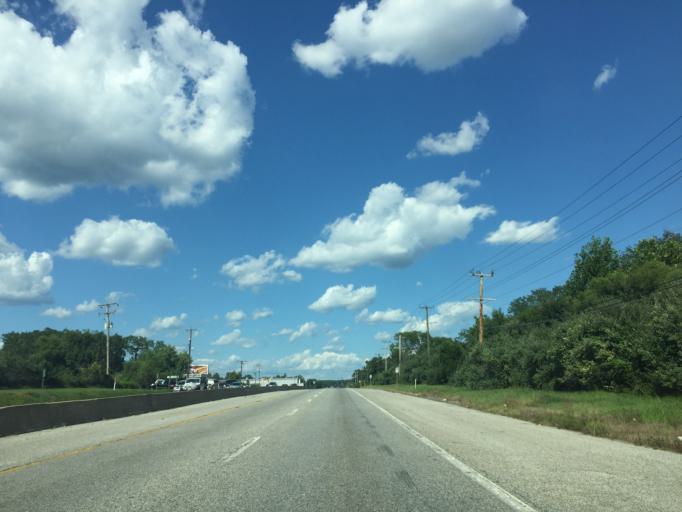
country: US
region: Maryland
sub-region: Baltimore County
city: Kingsville
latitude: 39.4119
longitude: -76.3858
